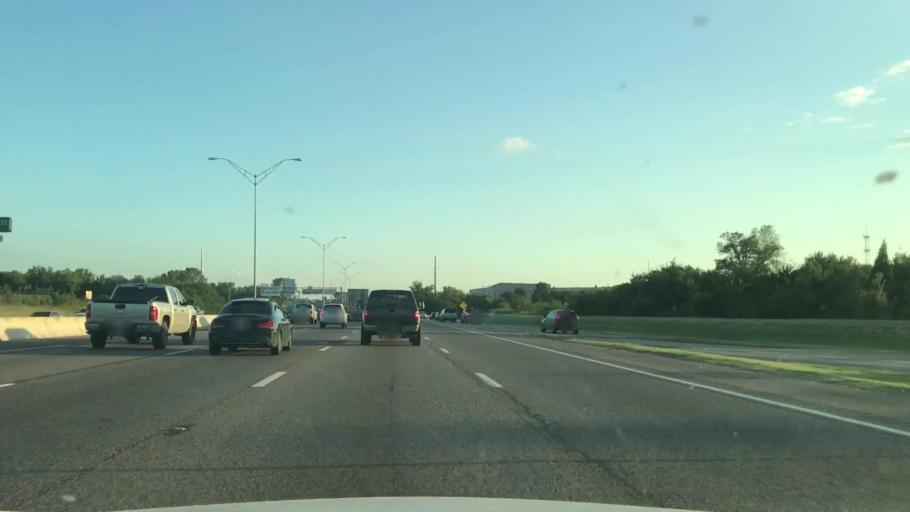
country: US
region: Texas
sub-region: Dallas County
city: Mesquite
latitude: 32.7790
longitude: -96.6244
